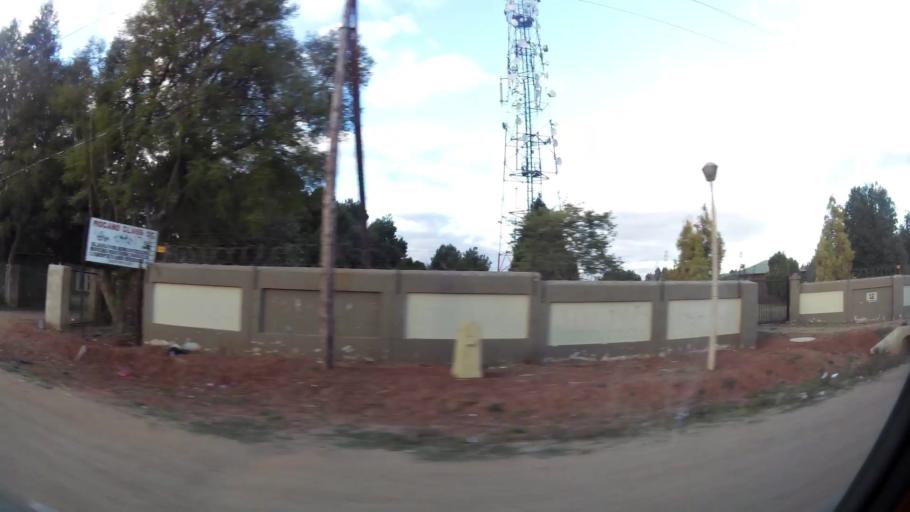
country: ZA
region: Gauteng
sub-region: City of Johannesburg Metropolitan Municipality
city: Midrand
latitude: -26.0061
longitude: 28.1586
